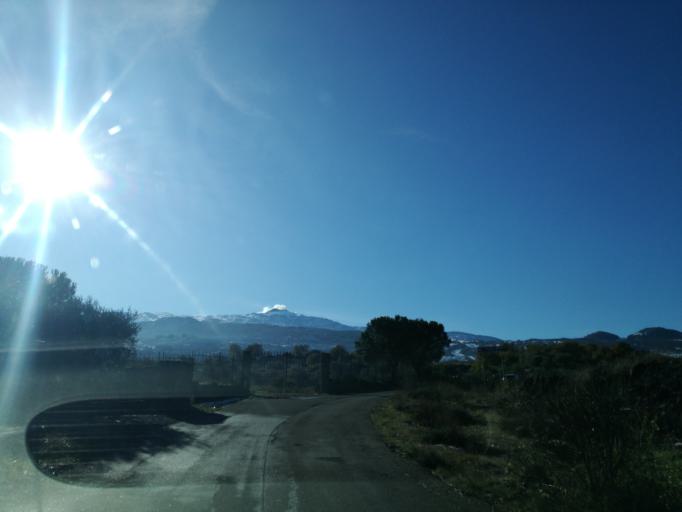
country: IT
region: Sicily
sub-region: Catania
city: Randazzo
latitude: 37.8652
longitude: 14.9801
